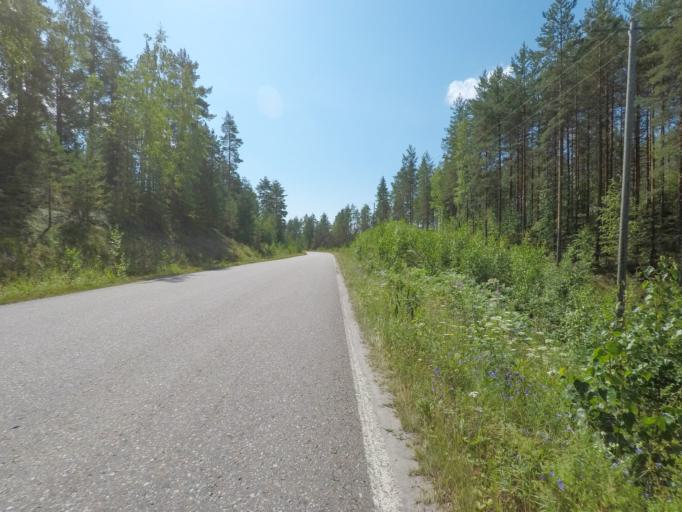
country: FI
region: Southern Savonia
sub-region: Mikkeli
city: Puumala
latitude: 61.5043
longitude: 28.1673
